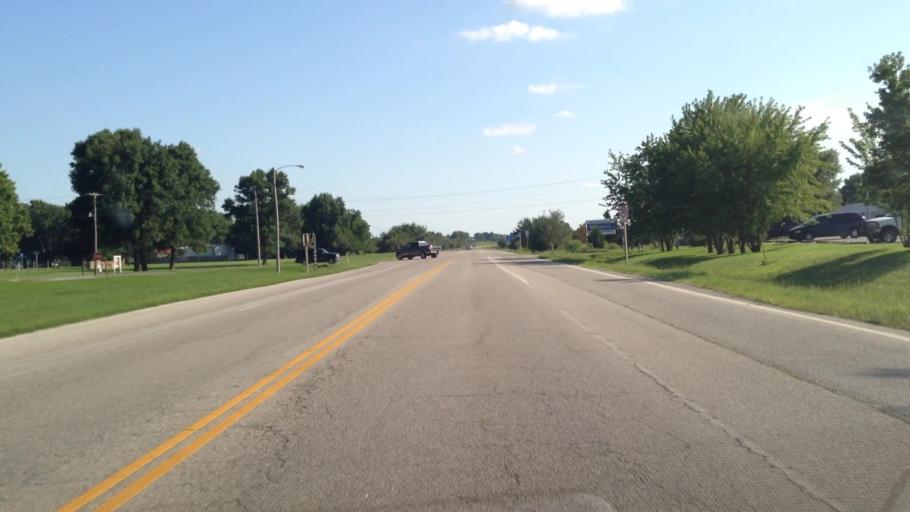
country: US
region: Kansas
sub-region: Crawford County
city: Arma
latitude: 37.5439
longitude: -94.7102
